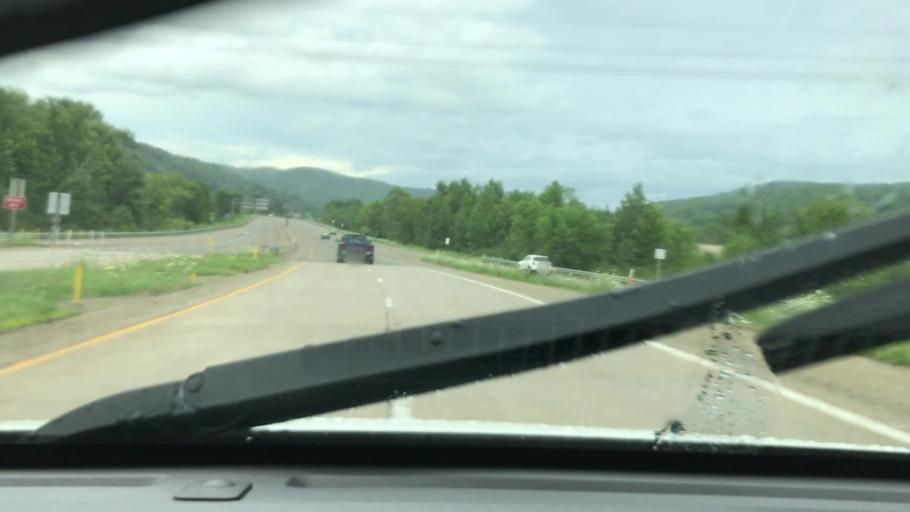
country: US
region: Pennsylvania
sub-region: McKean County
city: Bradford
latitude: 41.9311
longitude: -78.6486
